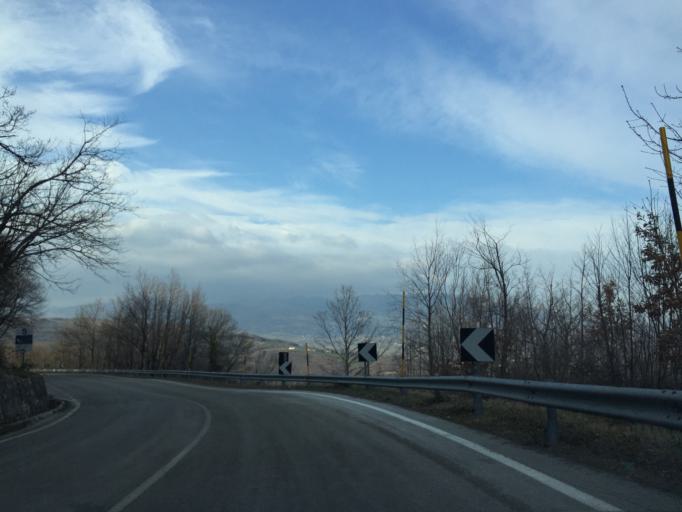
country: IT
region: Molise
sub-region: Provincia di Campobasso
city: San Massimo
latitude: 41.4849
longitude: 14.4098
